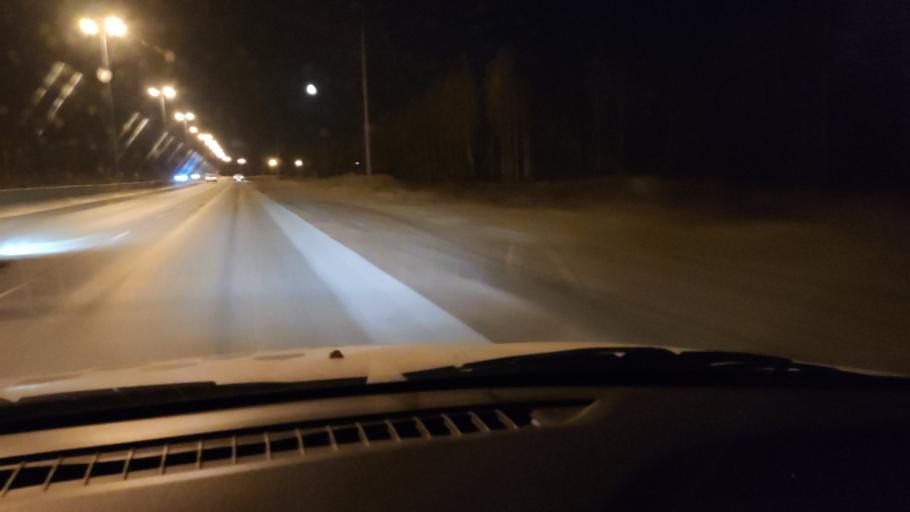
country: RU
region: Perm
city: Kondratovo
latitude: 58.0555
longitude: 56.0748
